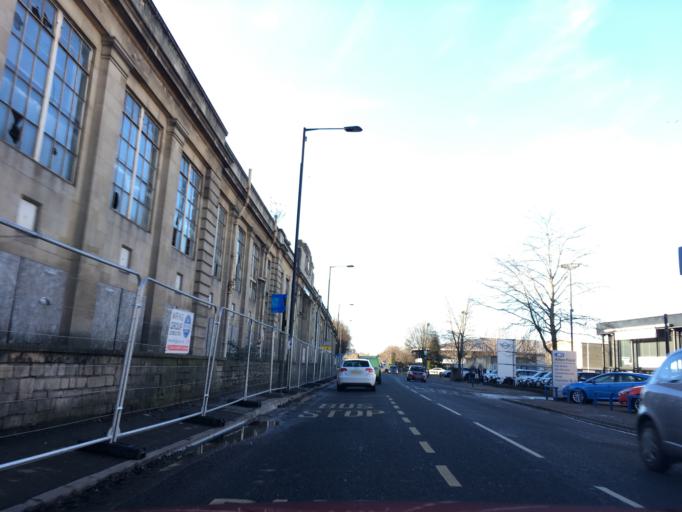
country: GB
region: England
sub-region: Bath and North East Somerset
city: Bath
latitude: 51.3816
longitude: -2.3776
